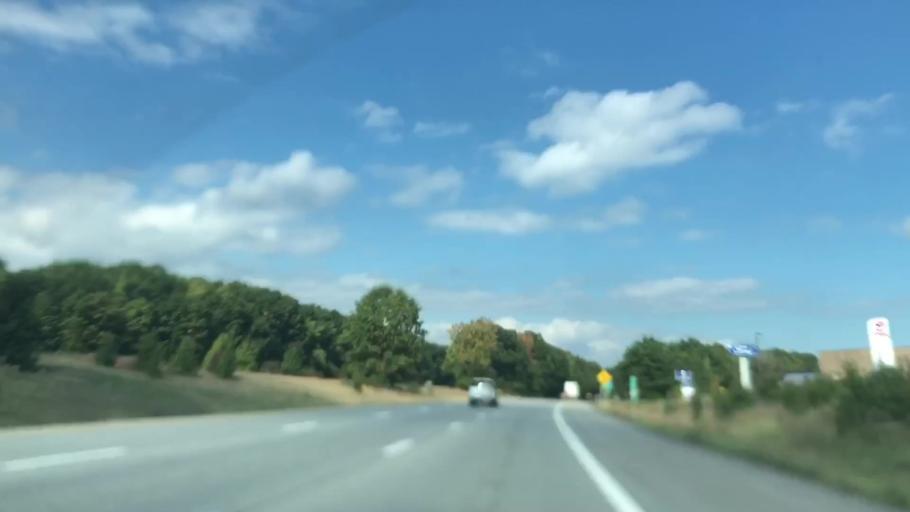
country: US
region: New York
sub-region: Saratoga County
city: Saratoga Springs
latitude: 43.0974
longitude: -73.7522
